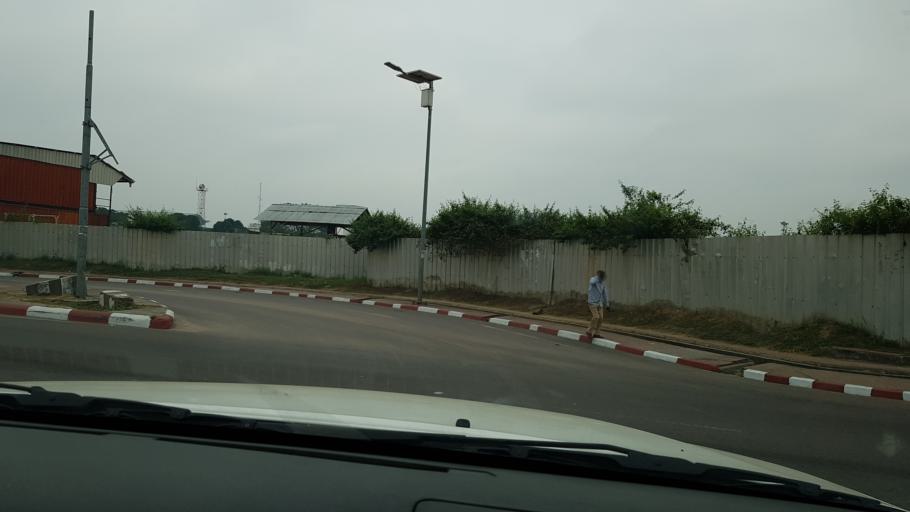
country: CG
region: Brazzaville
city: Brazzaville
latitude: -4.2581
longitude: 15.2557
